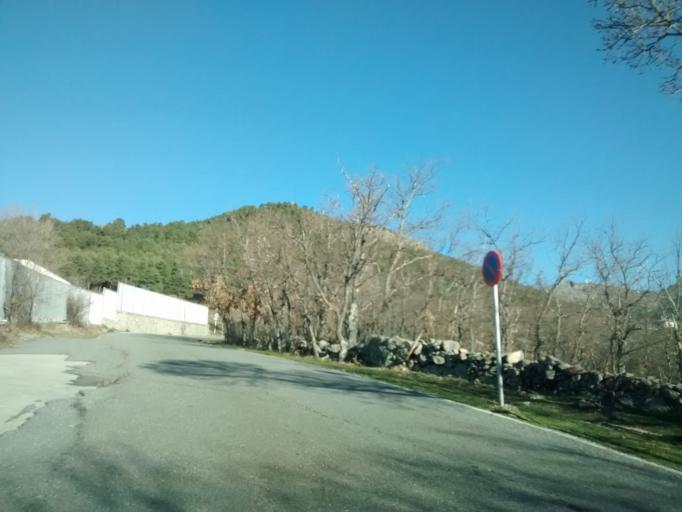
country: ES
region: Madrid
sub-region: Provincia de Madrid
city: Navacerrada
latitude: 40.7401
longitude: -4.0038
